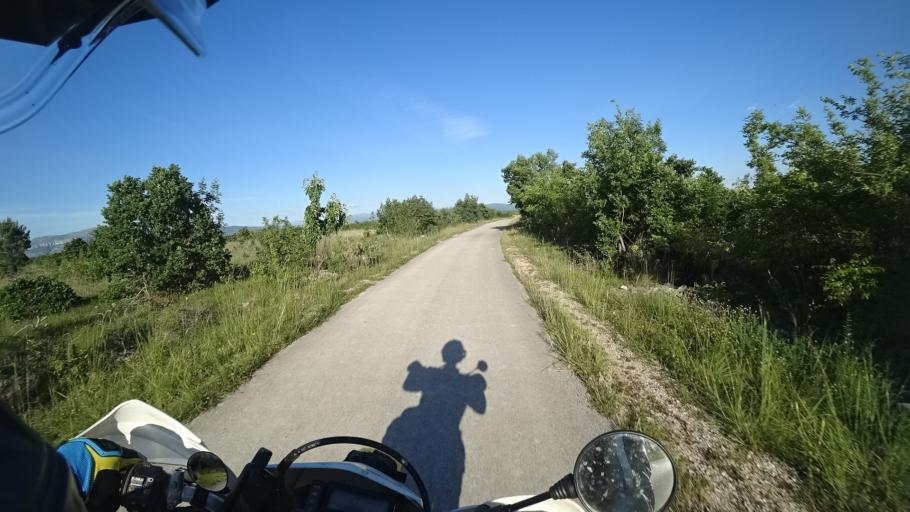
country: HR
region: Sibensko-Kniniska
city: Drnis
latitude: 43.8436
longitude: 16.0411
